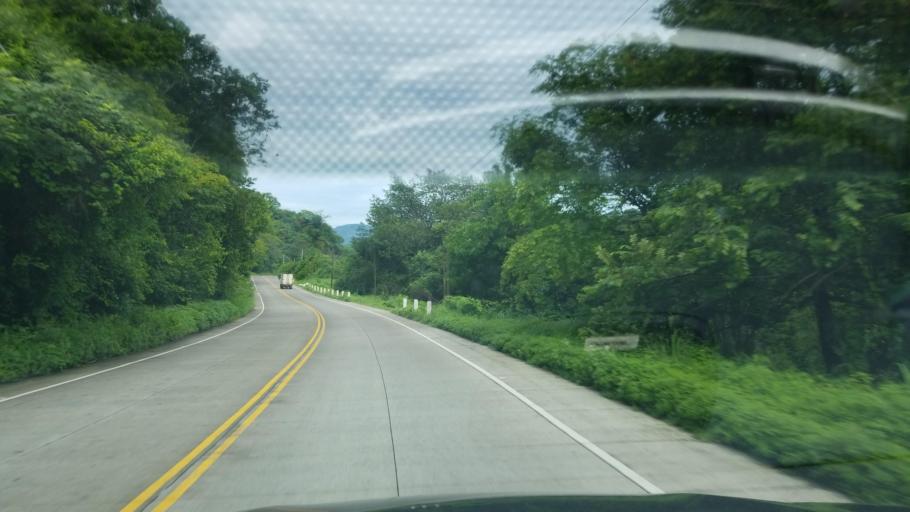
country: HN
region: Francisco Morazan
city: El Porvenir
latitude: 13.6857
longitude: -87.3494
